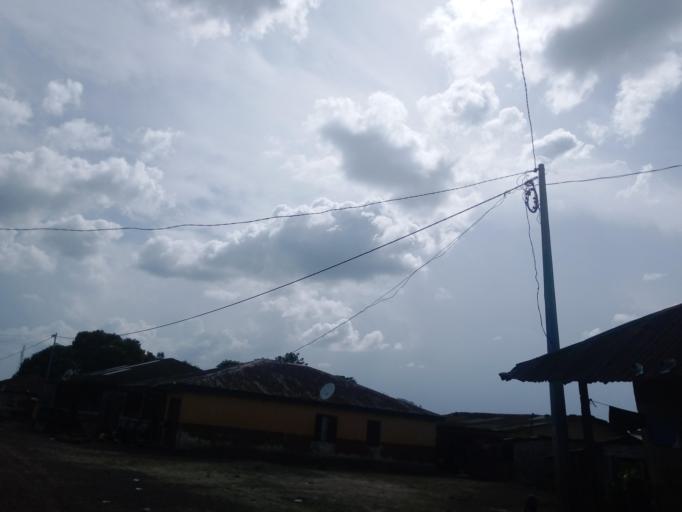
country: SL
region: Northern Province
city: Makeni
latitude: 8.8907
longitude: -12.0393
